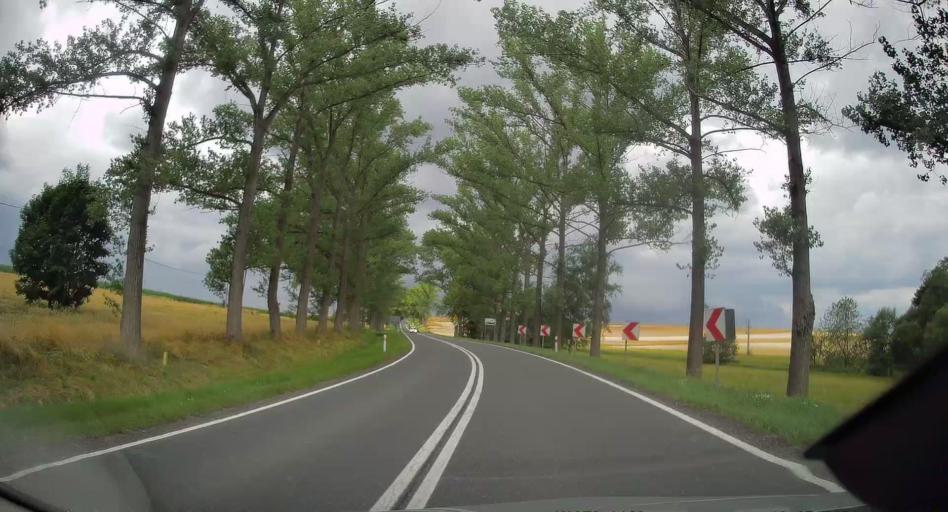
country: PL
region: Opole Voivodeship
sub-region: Powiat prudnicki
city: Laka Prudnicka
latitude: 50.3846
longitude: 17.5244
